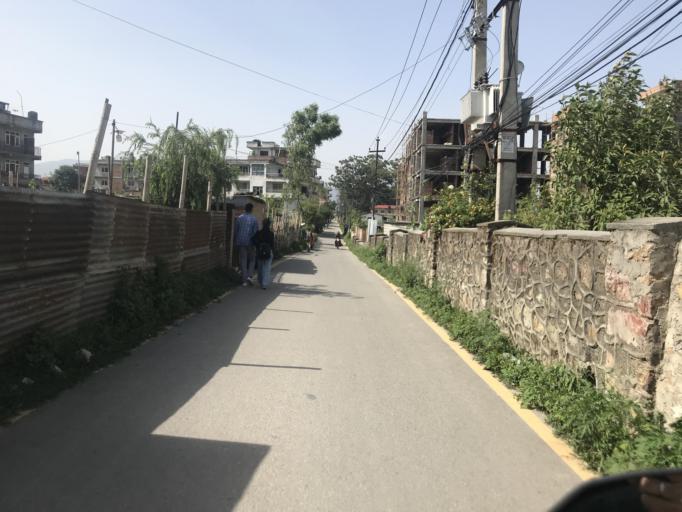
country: NP
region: Central Region
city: Kirtipur
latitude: 27.6781
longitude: 85.2816
